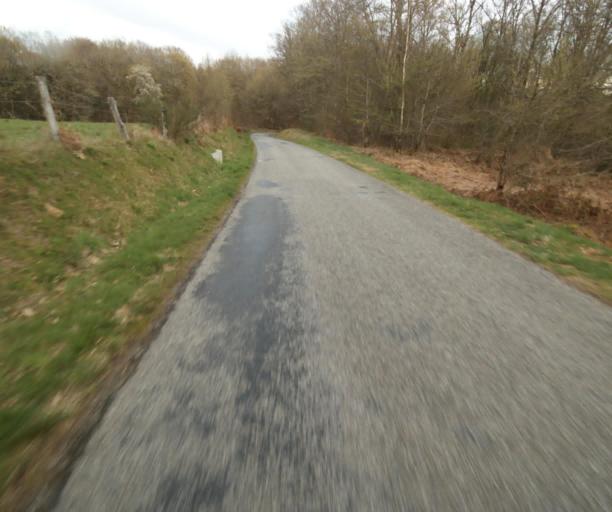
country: FR
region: Limousin
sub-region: Departement de la Correze
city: Argentat
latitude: 45.2280
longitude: 1.9814
